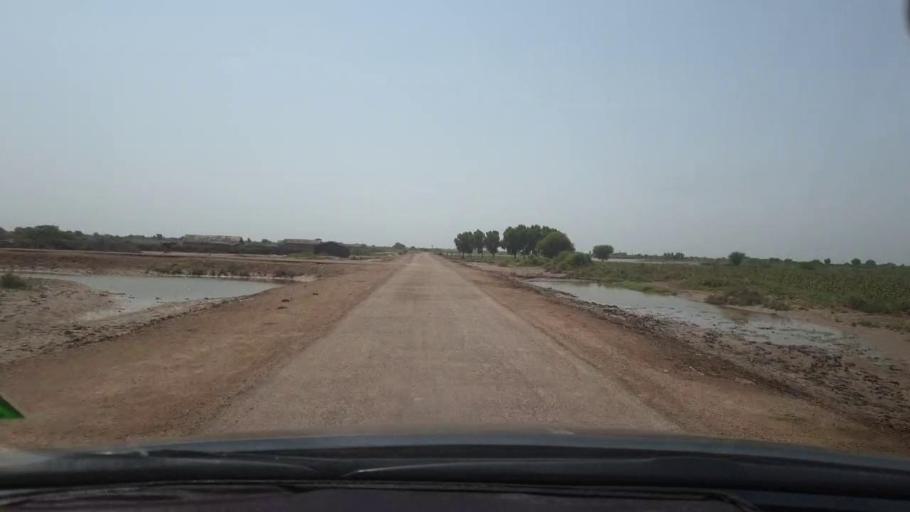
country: PK
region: Sindh
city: Tando Bago
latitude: 24.7987
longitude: 69.1682
